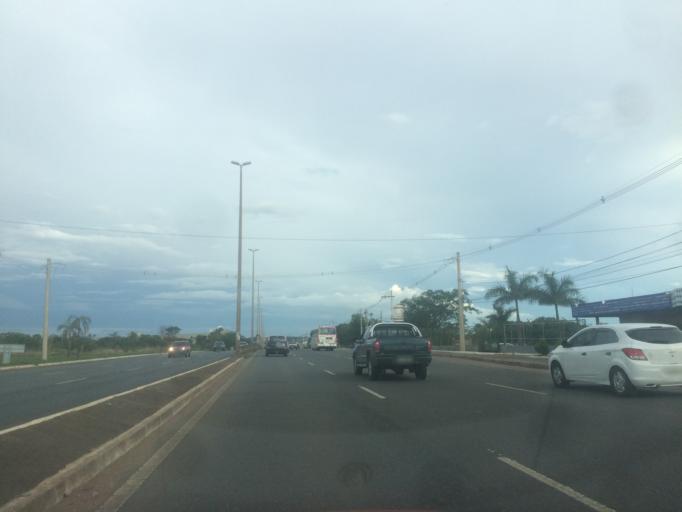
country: BR
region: Federal District
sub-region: Brasilia
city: Brasilia
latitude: -15.8129
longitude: -47.8440
